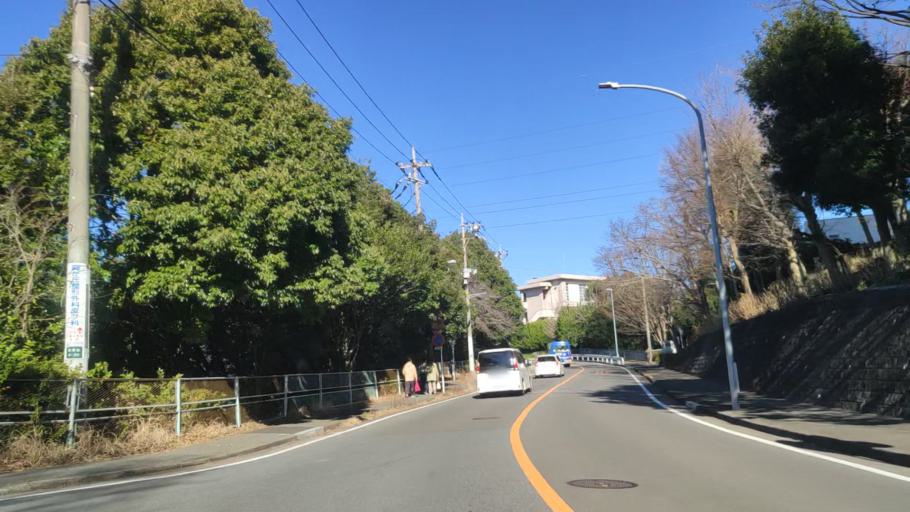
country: JP
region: Kanagawa
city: Minami-rinkan
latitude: 35.5078
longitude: 139.4983
